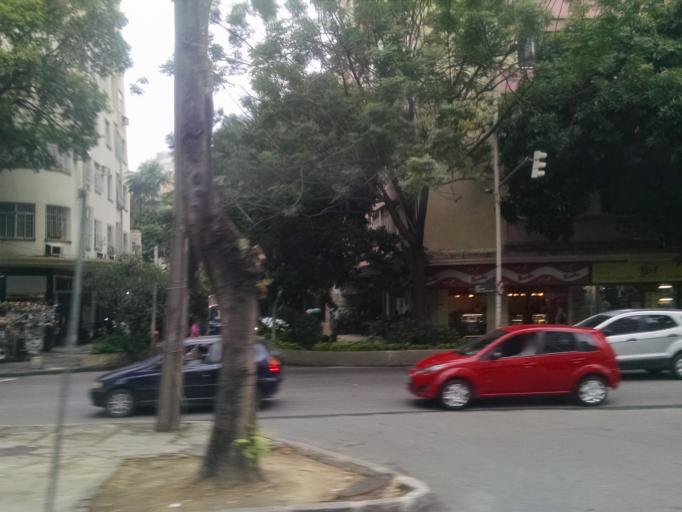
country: BR
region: Rio de Janeiro
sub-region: Rio De Janeiro
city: Rio de Janeiro
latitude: -22.9567
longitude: -43.1986
